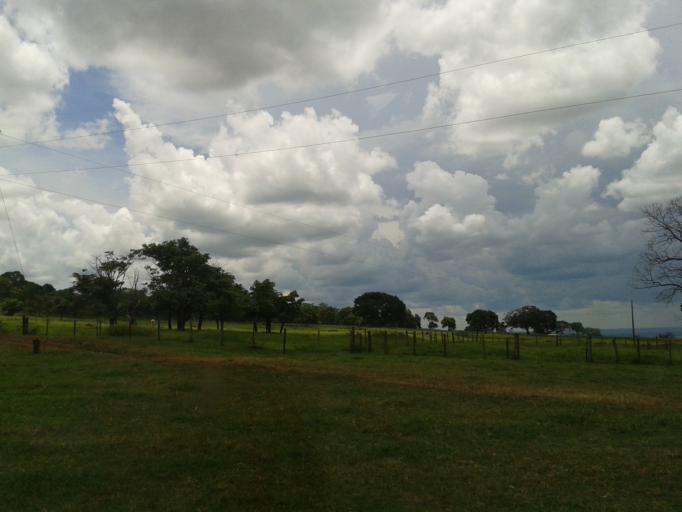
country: BR
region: Minas Gerais
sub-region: Centralina
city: Centralina
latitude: -18.6969
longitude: -49.2303
